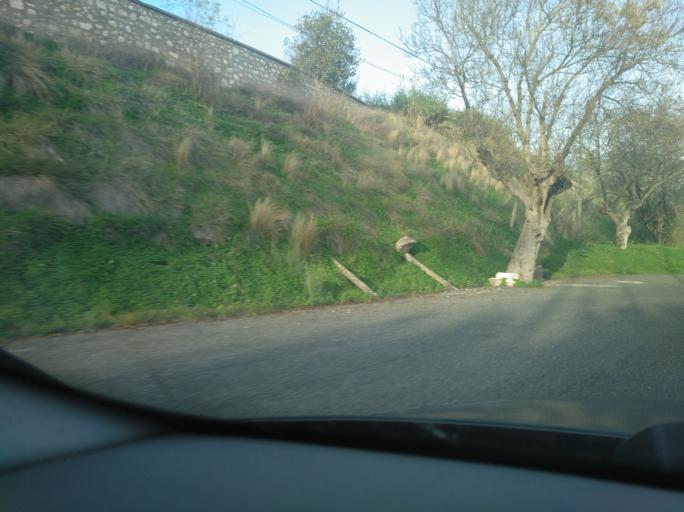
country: PT
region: Lisbon
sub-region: Odivelas
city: Odivelas
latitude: 38.7770
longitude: -9.1819
